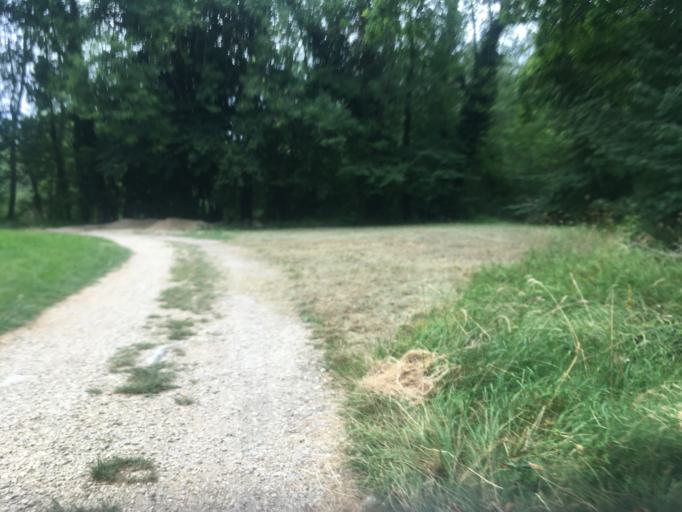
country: CH
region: Bern
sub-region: Jura bernois
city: La Neuveville
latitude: 47.0751
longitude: 7.1428
